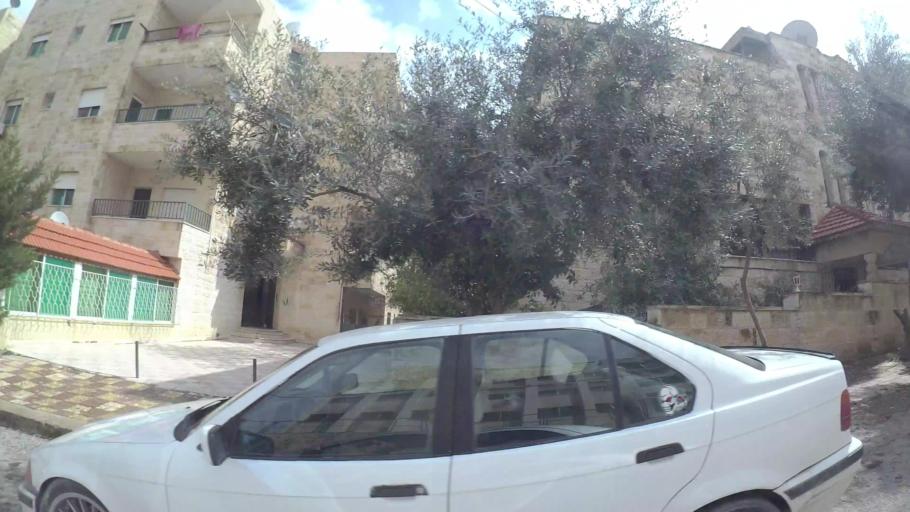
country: JO
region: Amman
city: Umm as Summaq
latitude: 31.8996
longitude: 35.8417
